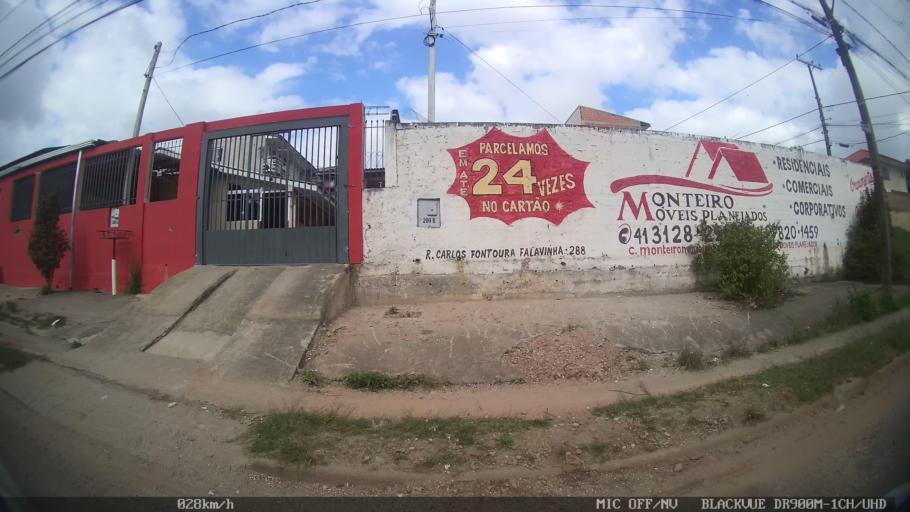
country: BR
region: Parana
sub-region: Colombo
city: Colombo
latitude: -25.3613
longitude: -49.1942
